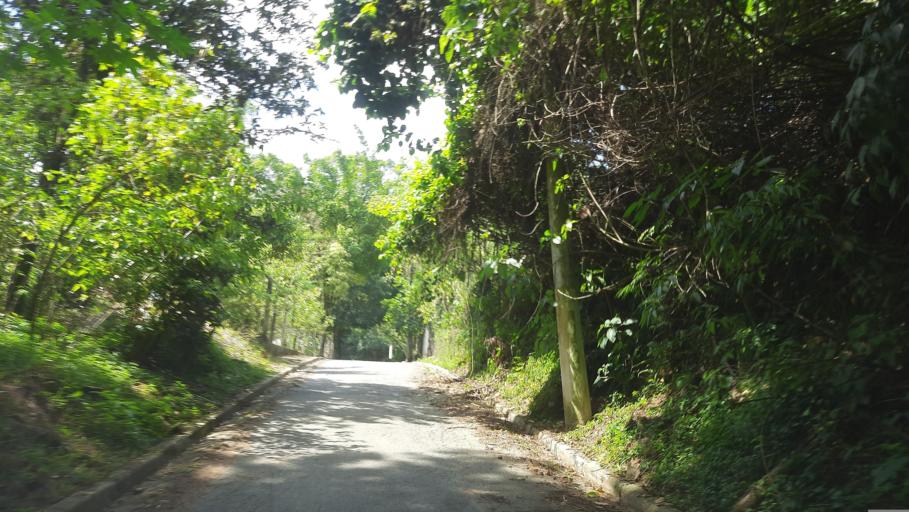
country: BR
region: Sao Paulo
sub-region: Caieiras
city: Caieiras
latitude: -23.4176
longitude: -46.7226
